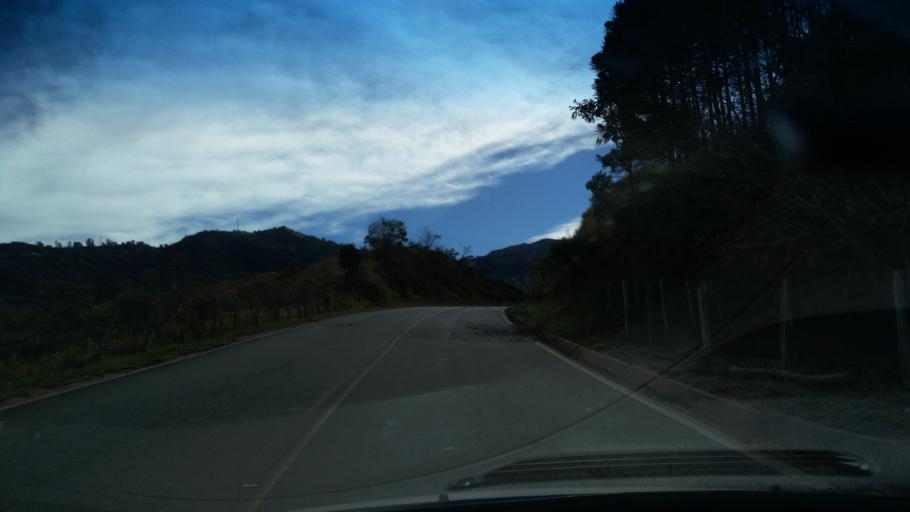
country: BR
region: Minas Gerais
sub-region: Andradas
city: Andradas
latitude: -22.0617
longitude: -46.4356
